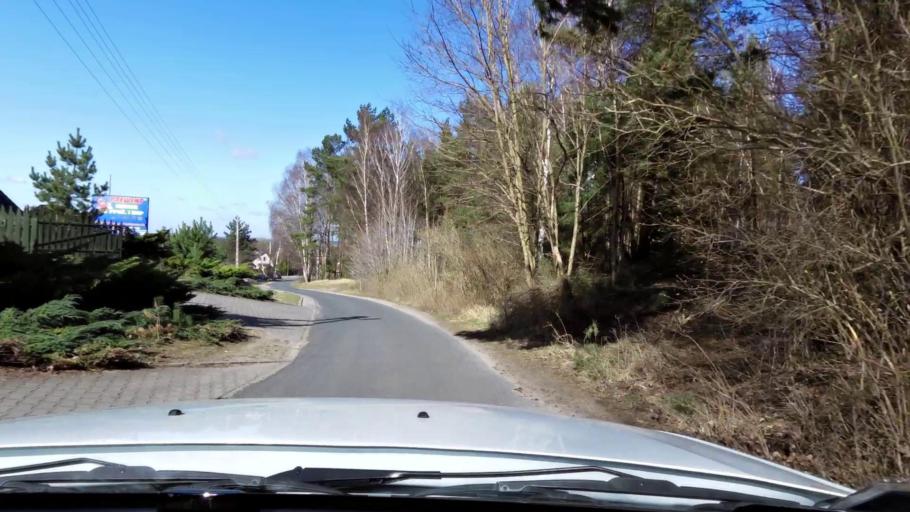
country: PL
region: West Pomeranian Voivodeship
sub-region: Powiat gryfinski
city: Gryfino
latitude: 53.2175
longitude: 14.5061
